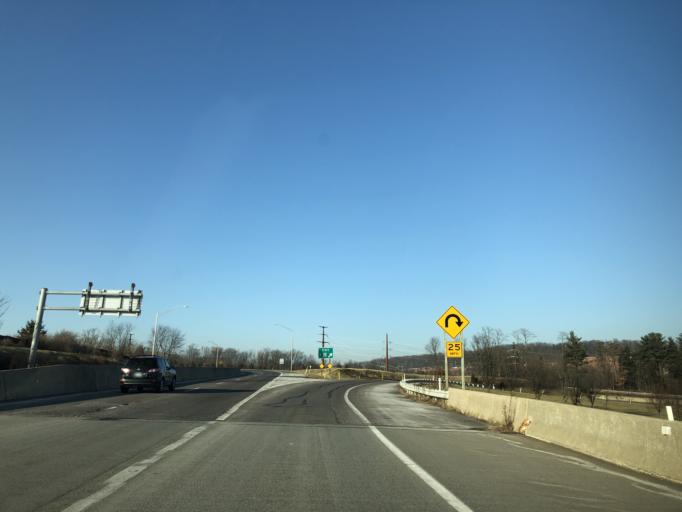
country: US
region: Pennsylvania
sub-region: Chester County
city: Elverson
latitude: 40.1640
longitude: -75.8830
